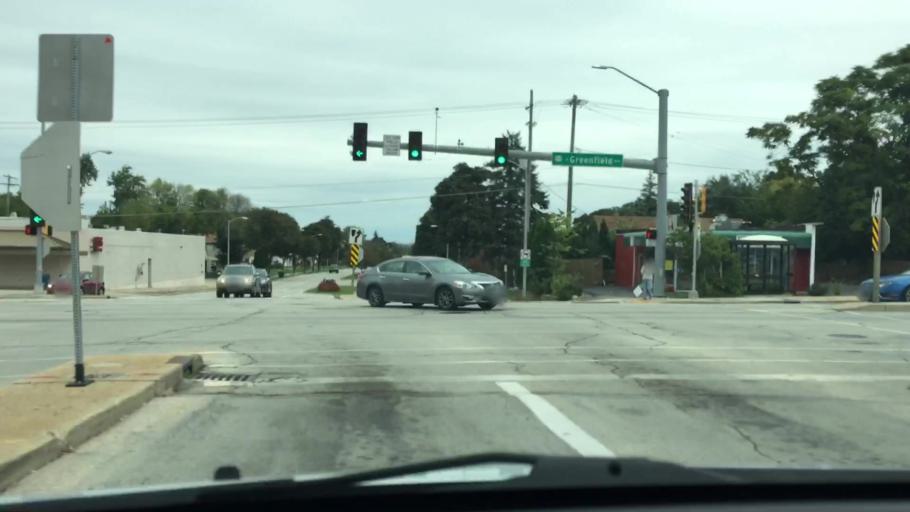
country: US
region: Wisconsin
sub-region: Milwaukee County
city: West Allis
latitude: 43.0164
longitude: -88.0271
